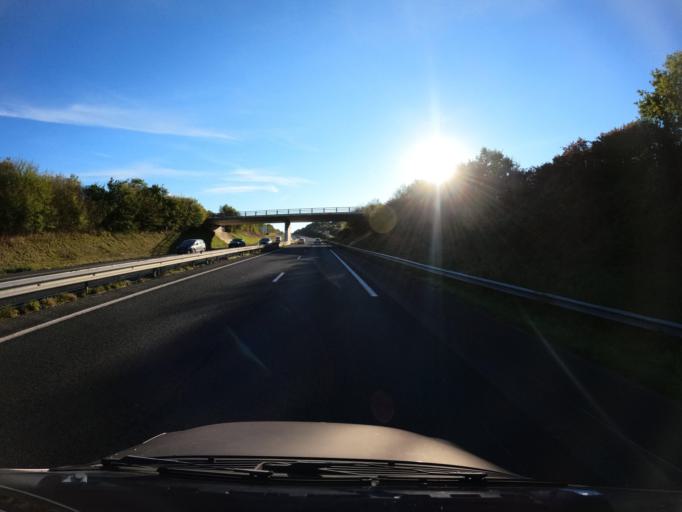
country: FR
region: Pays de la Loire
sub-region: Departement de Maine-et-Loire
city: La Tessoualle
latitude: 47.0301
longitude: -0.8606
